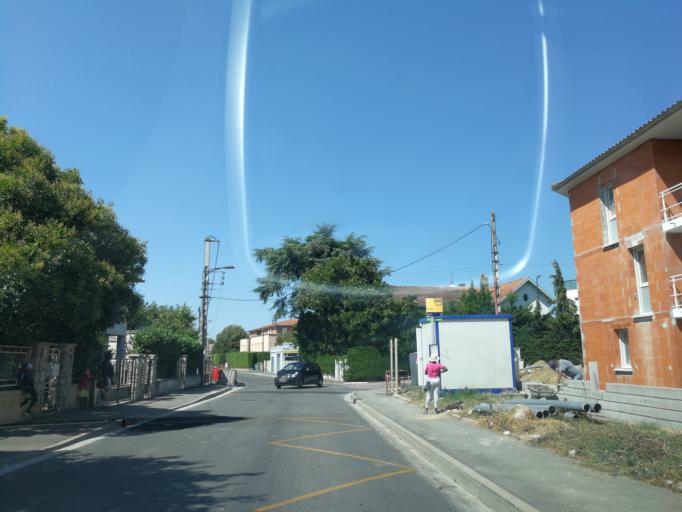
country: FR
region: Midi-Pyrenees
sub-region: Departement de la Haute-Garonne
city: L'Union
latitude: 43.6330
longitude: 1.4699
